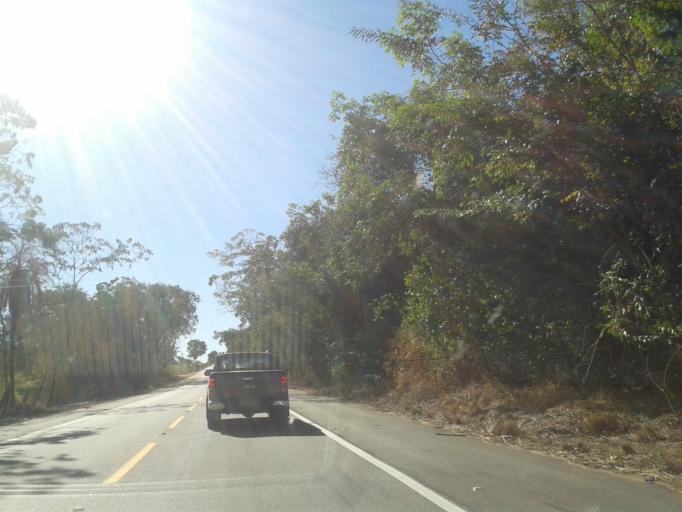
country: BR
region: Goias
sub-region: Itapuranga
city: Itapuranga
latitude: -15.5963
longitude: -50.2565
